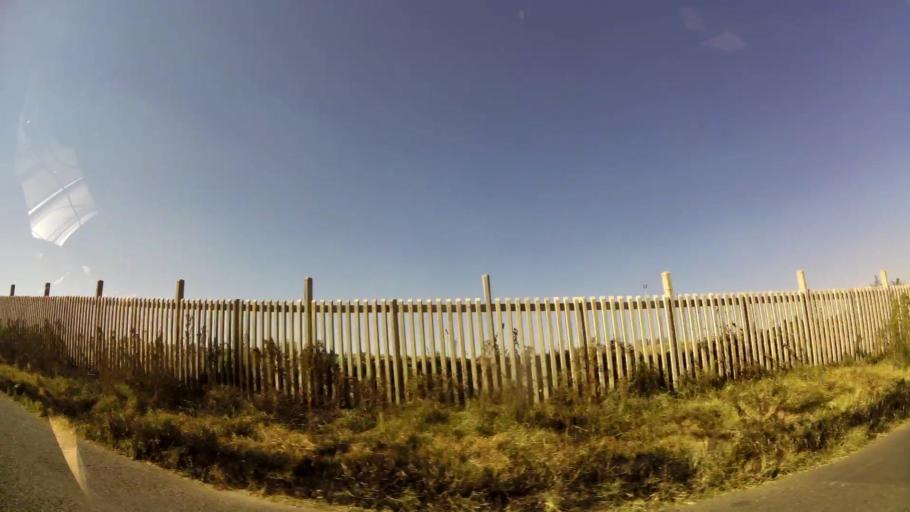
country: ZA
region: Gauteng
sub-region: City of Johannesburg Metropolitan Municipality
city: Johannesburg
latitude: -26.1793
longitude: 27.9688
